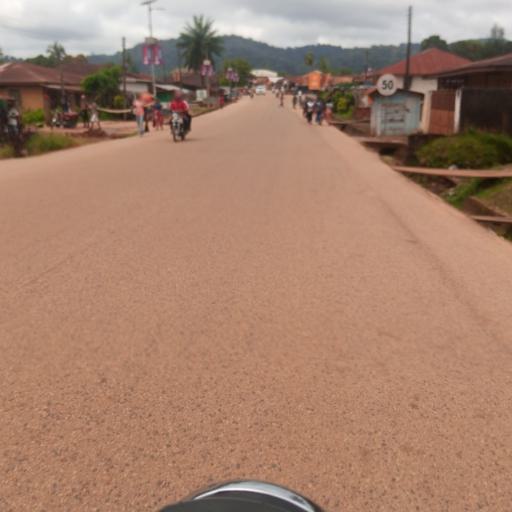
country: SL
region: Eastern Province
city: Kenema
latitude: 7.8763
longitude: -11.1859
